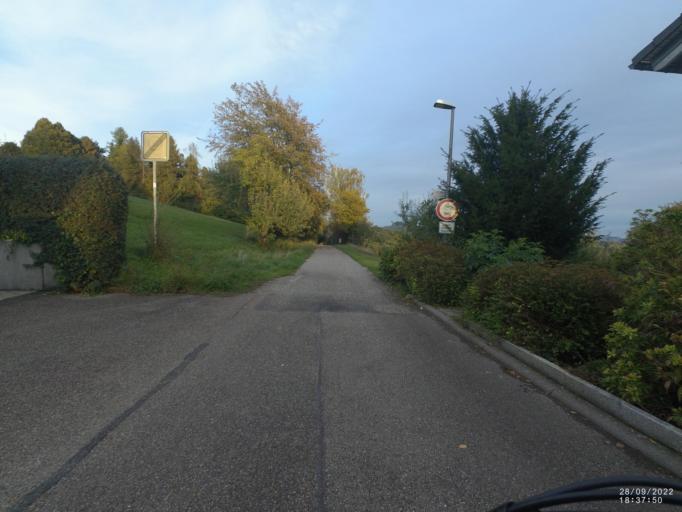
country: DE
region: Baden-Wuerttemberg
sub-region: Regierungsbezirk Stuttgart
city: Bortlingen
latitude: 48.7521
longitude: 9.6370
